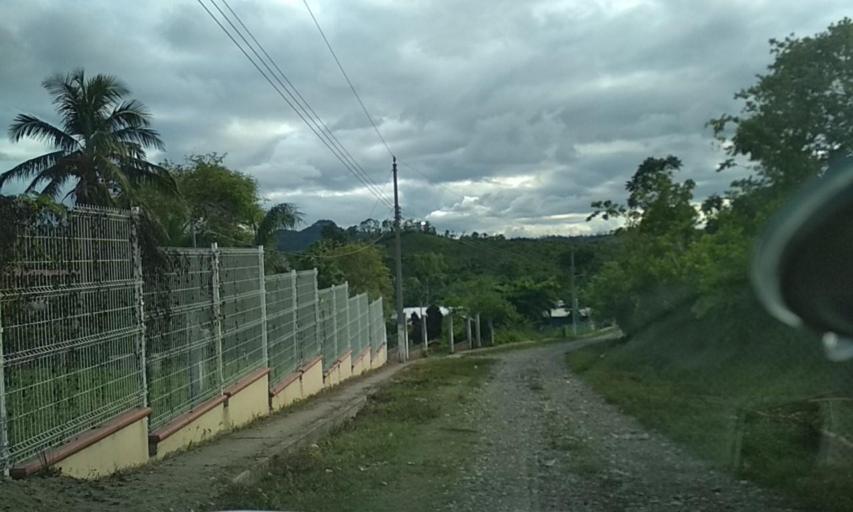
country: MX
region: Veracruz
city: Cazones de Herrera
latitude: 20.6499
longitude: -97.3370
